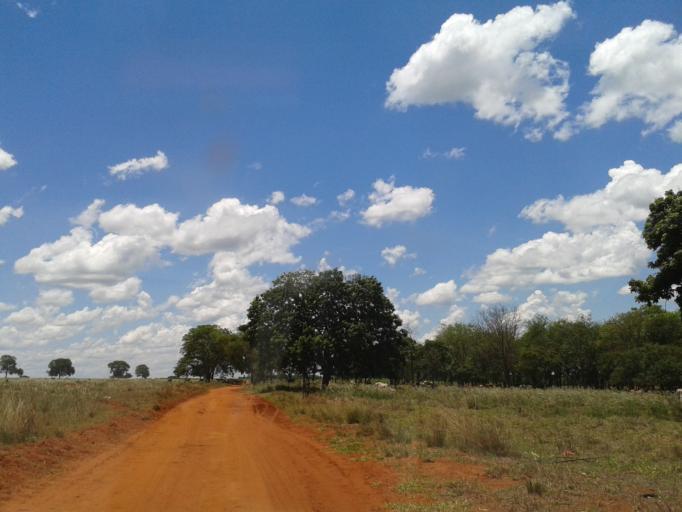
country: BR
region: Minas Gerais
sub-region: Centralina
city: Centralina
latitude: -18.7111
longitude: -49.1762
